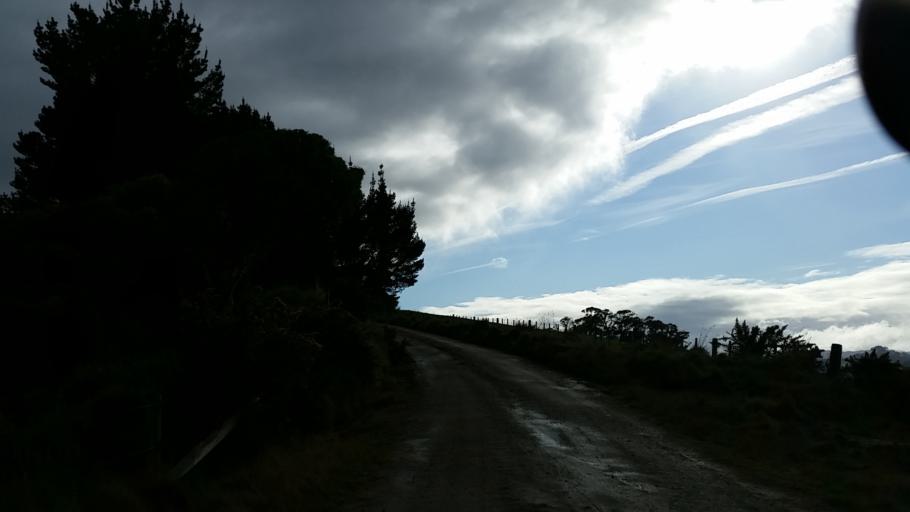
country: NZ
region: Taranaki
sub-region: South Taranaki District
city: Patea
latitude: -39.7243
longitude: 174.7157
